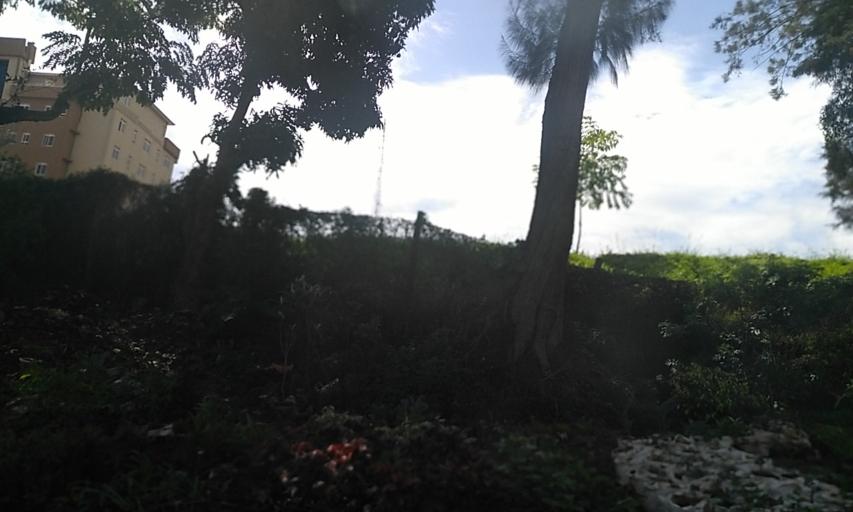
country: UG
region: Central Region
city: Kampala Central Division
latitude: 0.3411
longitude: 32.5936
